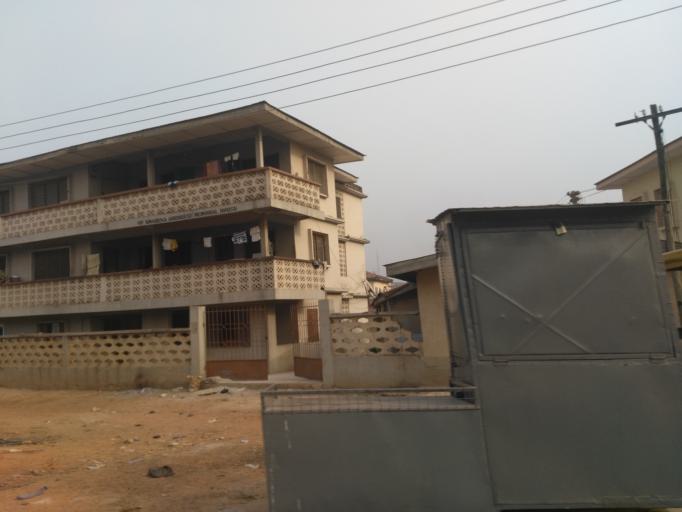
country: GH
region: Ashanti
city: Kumasi
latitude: 6.6950
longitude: -1.6117
